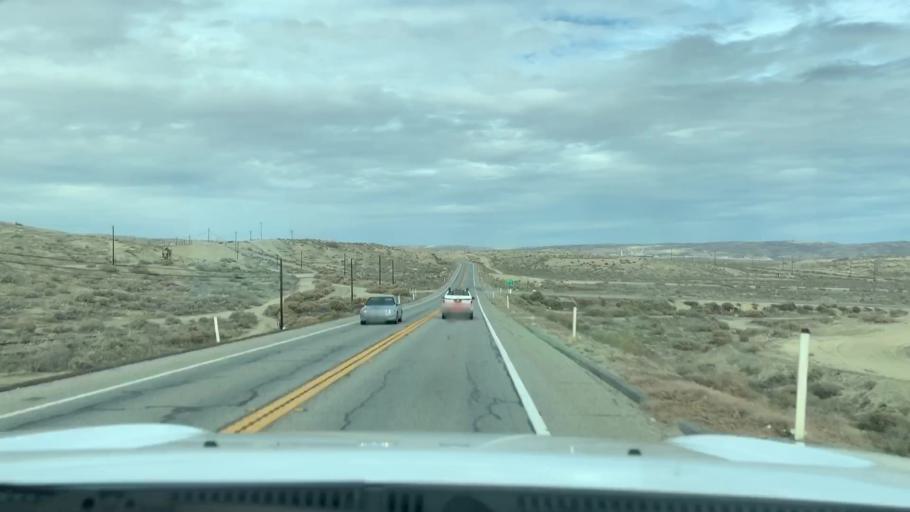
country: US
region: California
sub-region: Kern County
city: Maricopa
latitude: 35.0823
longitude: -119.4011
